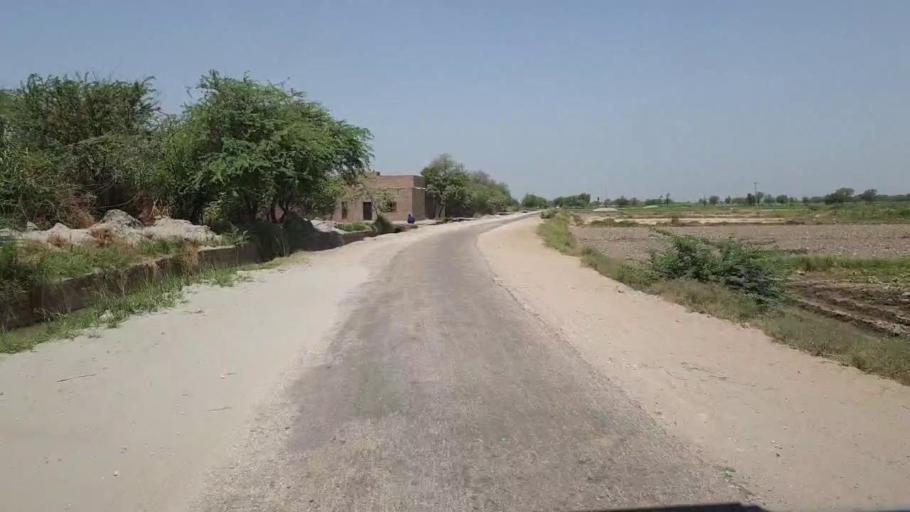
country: PK
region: Sindh
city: Nawabshah
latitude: 26.3429
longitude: 68.3664
